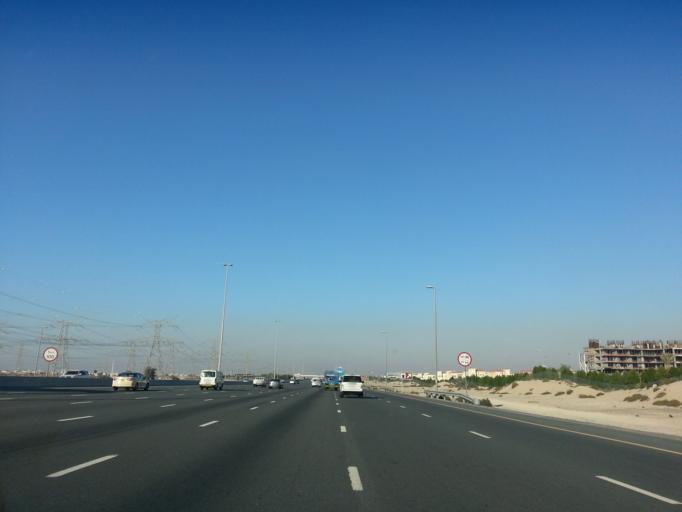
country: AE
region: Dubai
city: Dubai
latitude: 25.0690
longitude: 55.2038
